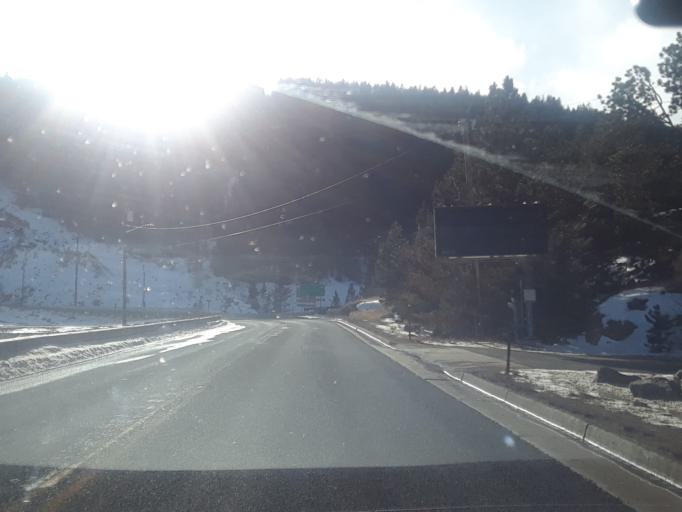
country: US
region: Colorado
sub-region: Gilpin County
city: Central City
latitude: 39.7972
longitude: -105.5159
